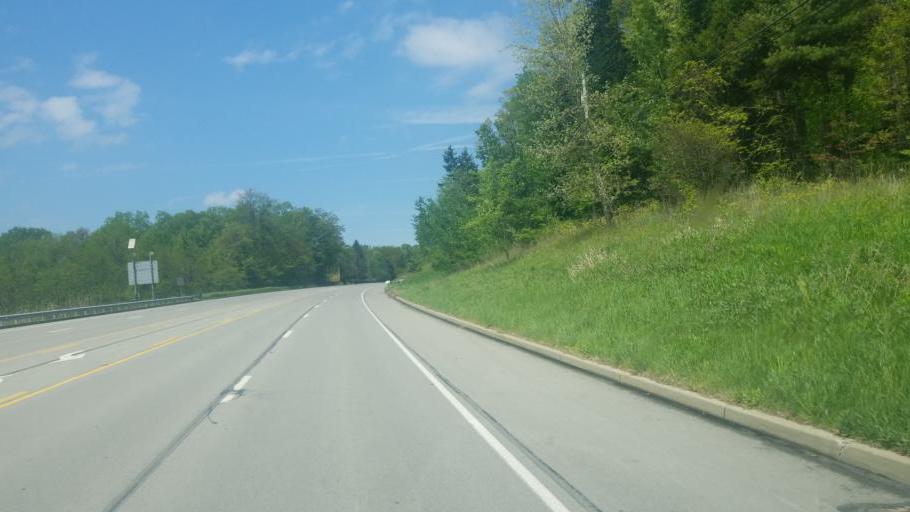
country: US
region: Pennsylvania
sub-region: Mercer County
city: Hermitage
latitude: 41.2119
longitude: -80.4569
